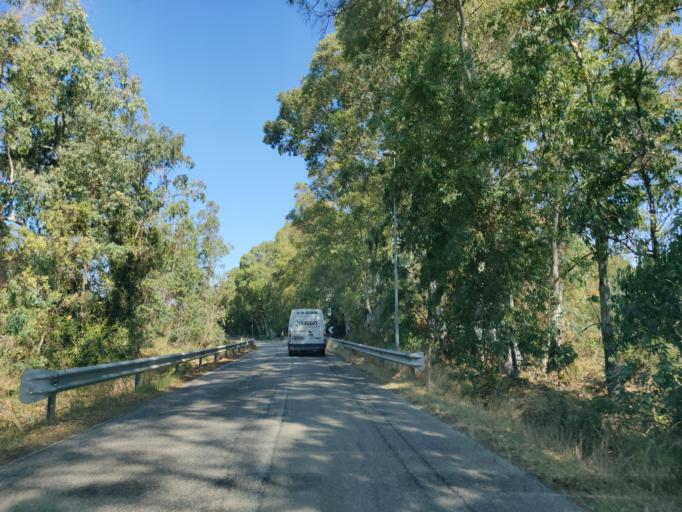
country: IT
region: Latium
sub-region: Citta metropolitana di Roma Capitale
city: Aurelia
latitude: 42.1488
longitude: 11.7696
